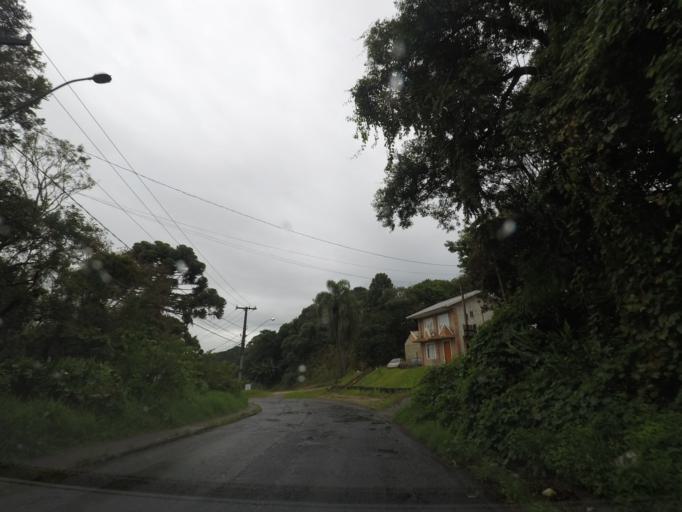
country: BR
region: Parana
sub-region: Campo Largo
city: Campo Largo
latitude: -25.4626
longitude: -49.4006
